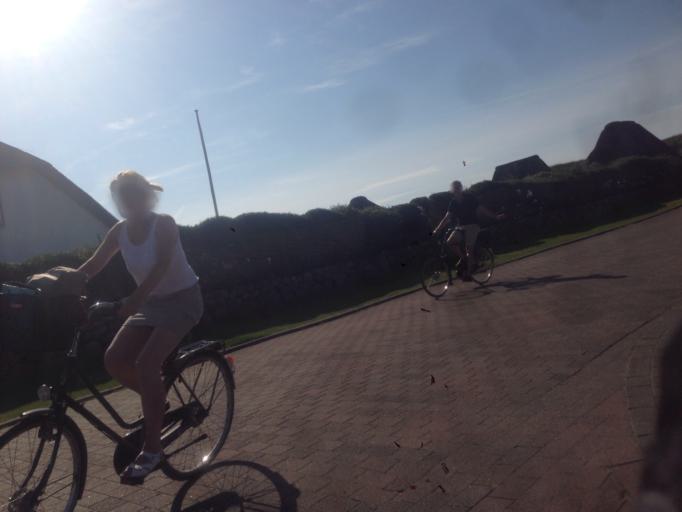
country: DE
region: Schleswig-Holstein
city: Westerland
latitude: 54.9339
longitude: 8.3164
